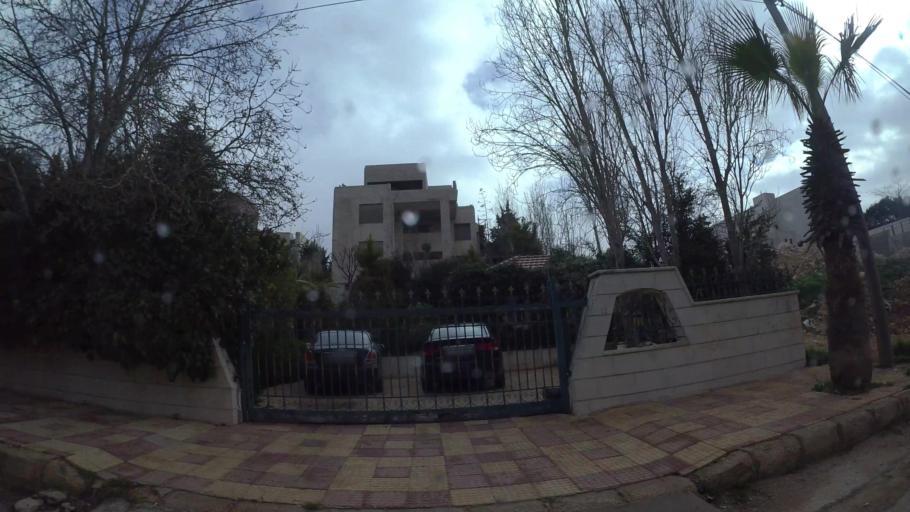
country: JO
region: Amman
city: Wadi as Sir
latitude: 31.9873
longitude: 35.8179
